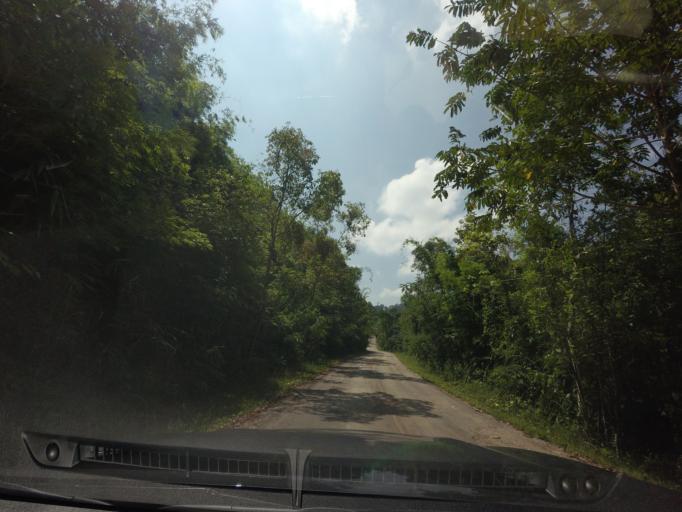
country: TH
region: Loei
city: Na Haeo
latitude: 17.5256
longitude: 100.9378
